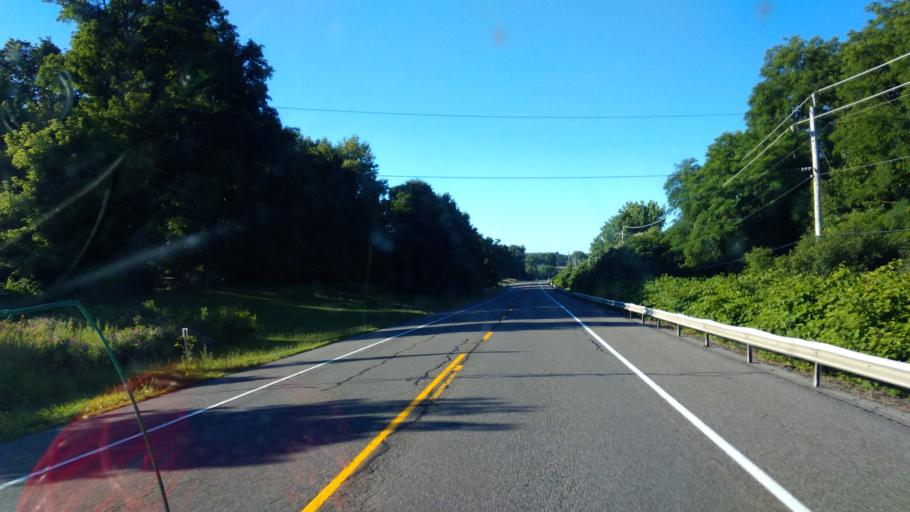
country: US
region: New York
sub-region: Wayne County
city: Lyons
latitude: 43.0030
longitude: -76.9810
